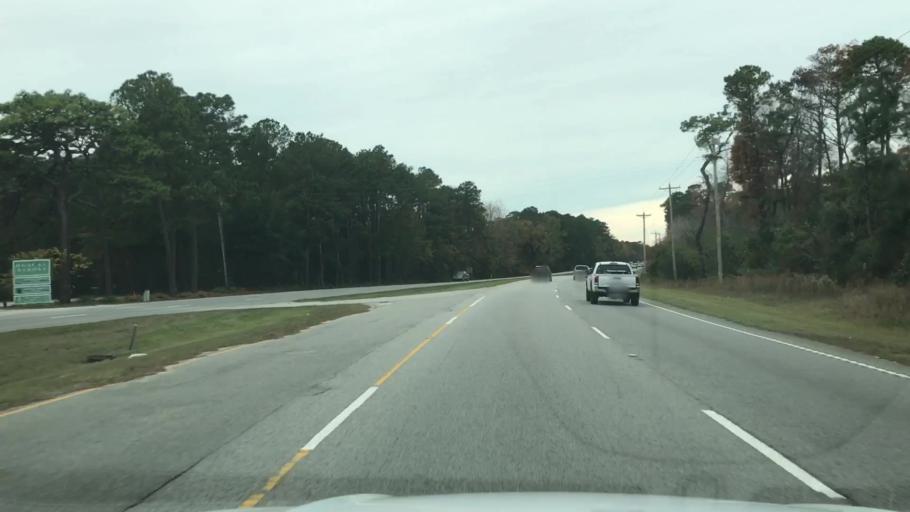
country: US
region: South Carolina
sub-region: Georgetown County
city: Georgetown
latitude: 33.3647
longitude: -79.2266
